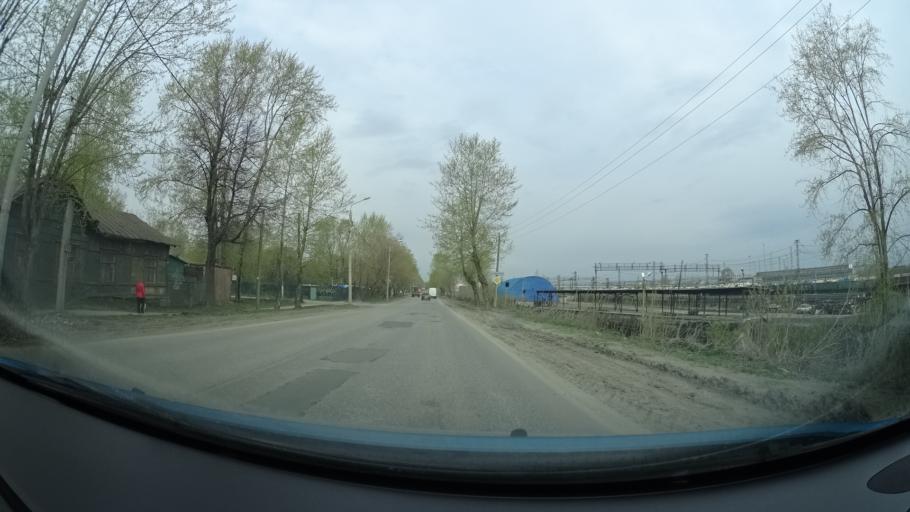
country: RU
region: Perm
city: Kondratovo
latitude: 58.0021
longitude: 56.1768
